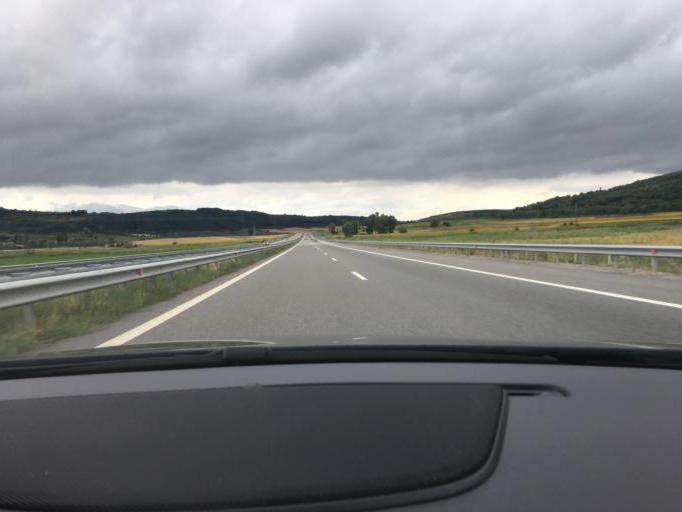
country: BG
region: Kyustendil
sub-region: Obshtina Bobovdol
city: Bobovdol
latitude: 42.4109
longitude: 23.1203
